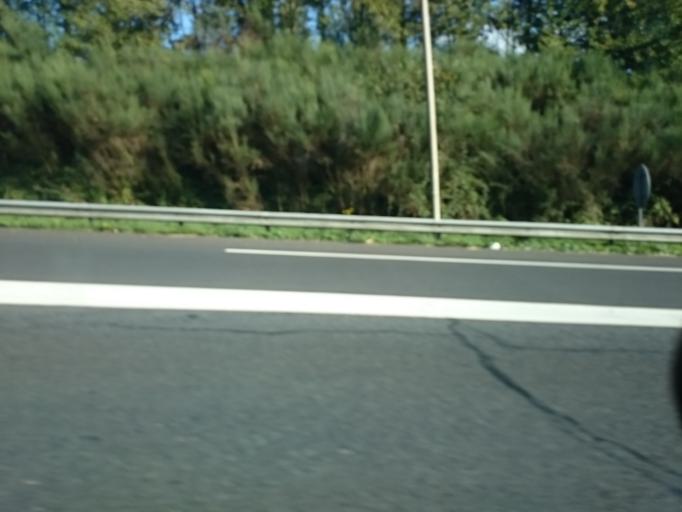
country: FR
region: Pays de la Loire
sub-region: Departement de la Loire-Atlantique
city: Saint-Herblain
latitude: 47.2177
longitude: -1.6244
